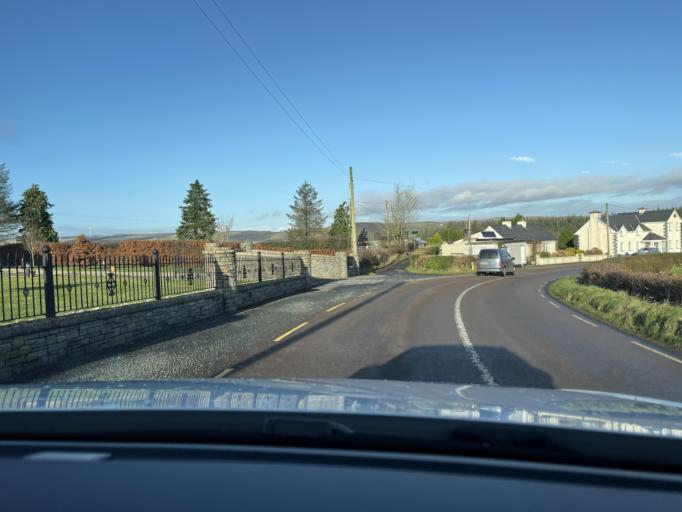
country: IE
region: Connaught
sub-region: County Leitrim
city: Manorhamilton
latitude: 54.3016
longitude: -8.2455
